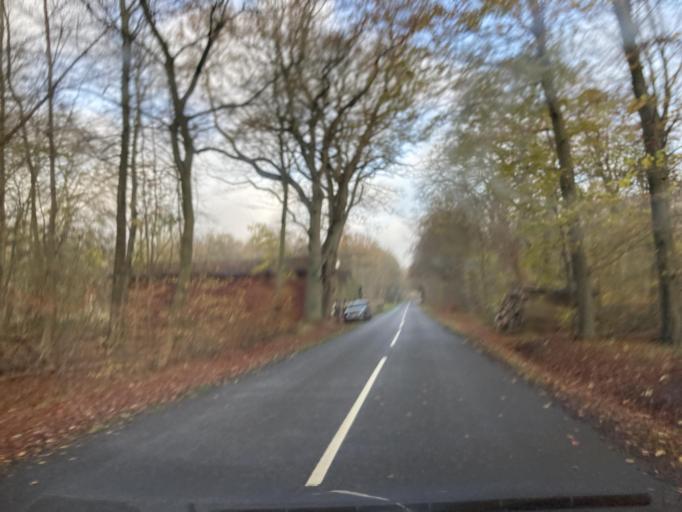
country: DK
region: Zealand
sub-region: Lolland Kommune
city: Rodby
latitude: 54.7748
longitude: 11.3666
